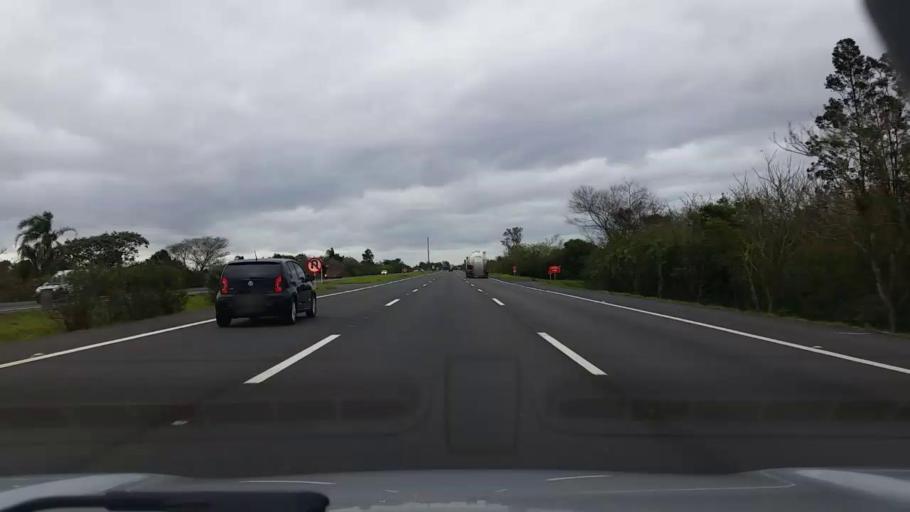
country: BR
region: Rio Grande do Sul
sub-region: Rolante
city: Rolante
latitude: -29.8837
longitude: -50.5579
